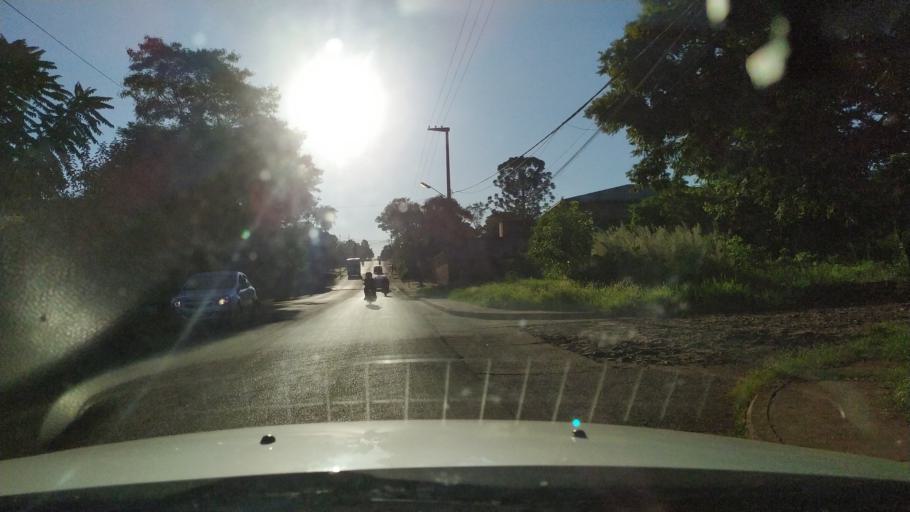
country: AR
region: Misiones
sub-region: Departamento de Eldorado
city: Eldorado
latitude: -26.4148
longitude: -54.6239
